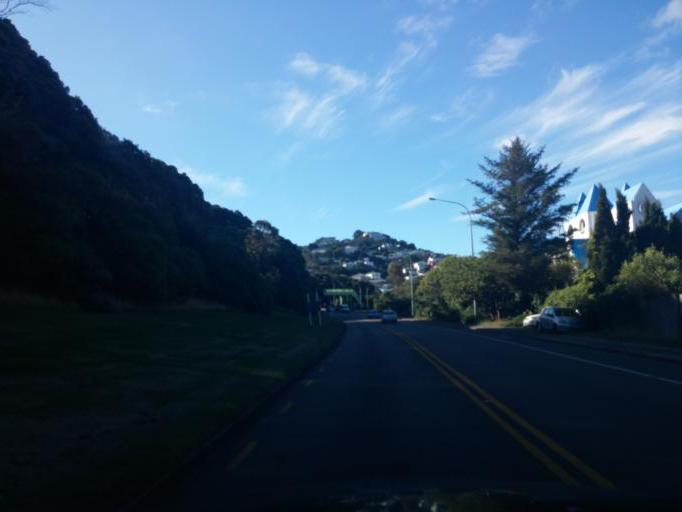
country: NZ
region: Wellington
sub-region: Wellington City
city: Wellington
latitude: -41.3066
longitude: 174.7923
